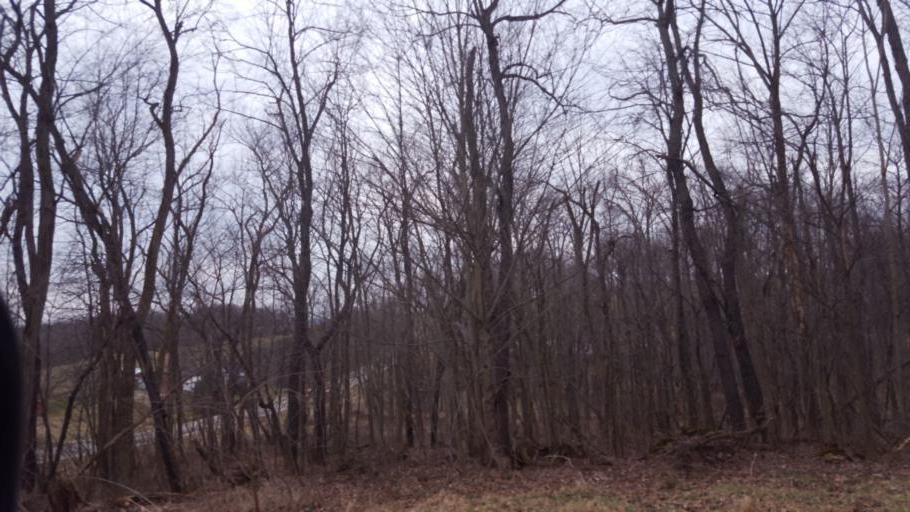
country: US
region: Ohio
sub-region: Ashland County
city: Loudonville
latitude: 40.6975
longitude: -82.2581
